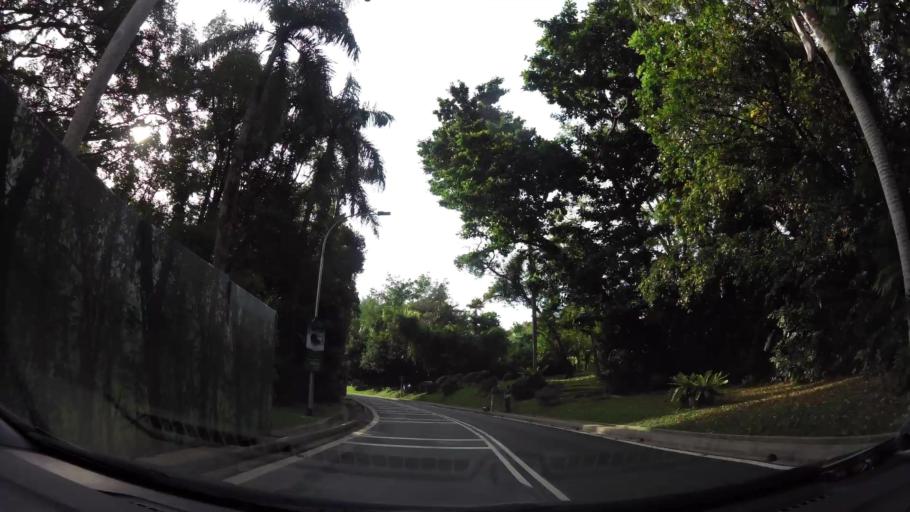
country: SG
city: Singapore
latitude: 1.2473
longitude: 103.8278
